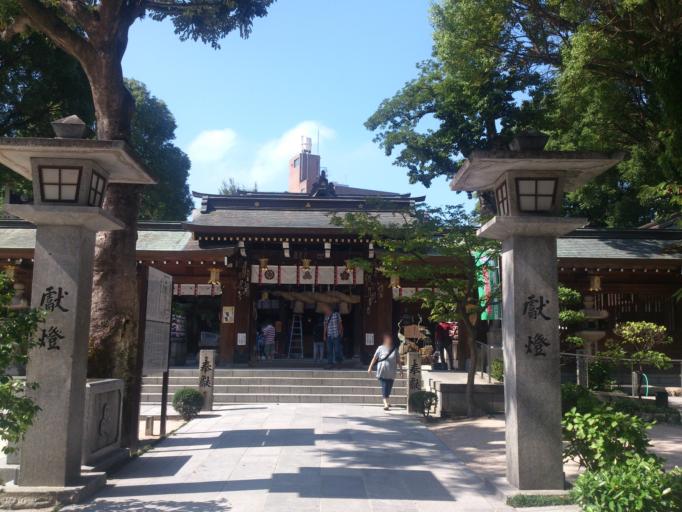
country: JP
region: Fukuoka
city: Fukuoka-shi
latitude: 33.5932
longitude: 130.4108
